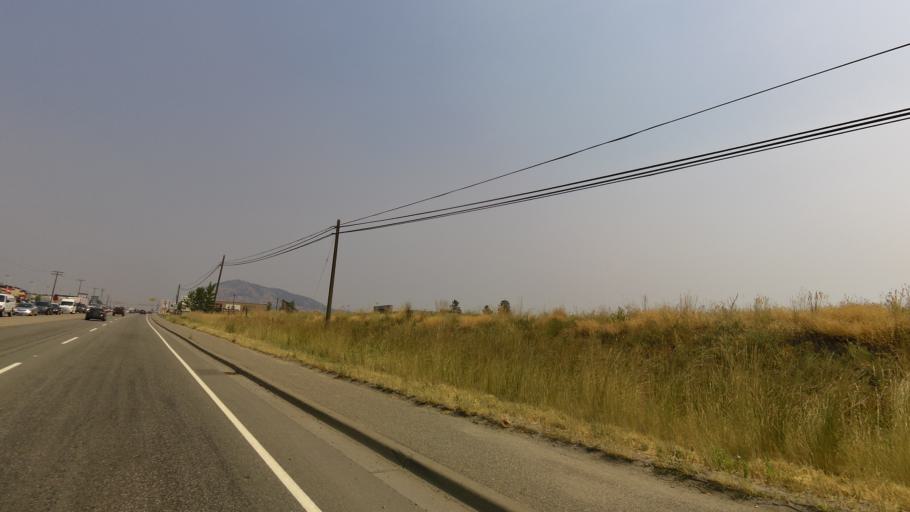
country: CA
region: British Columbia
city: West Kelowna
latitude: 49.8334
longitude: -119.6194
